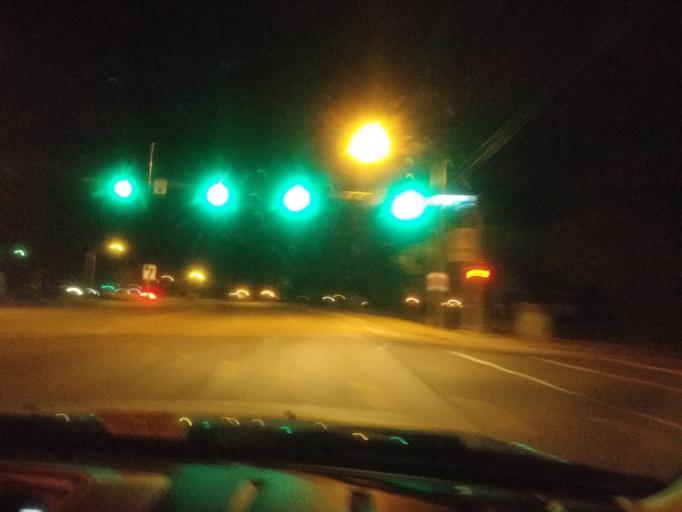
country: US
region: Virginia
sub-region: City of Chesapeake
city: Chesapeake
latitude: 36.7696
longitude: -76.2038
